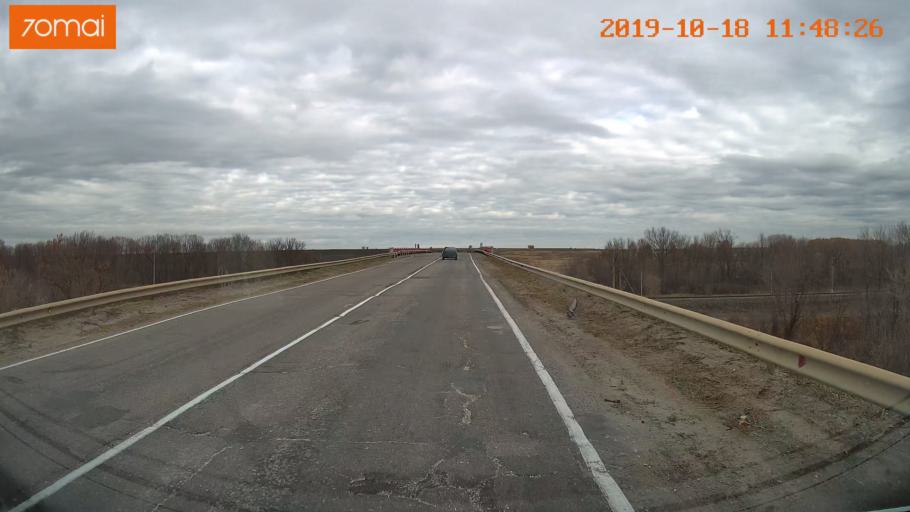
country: RU
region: Rjazan
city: Mikhaylov
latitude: 54.2395
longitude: 38.9827
